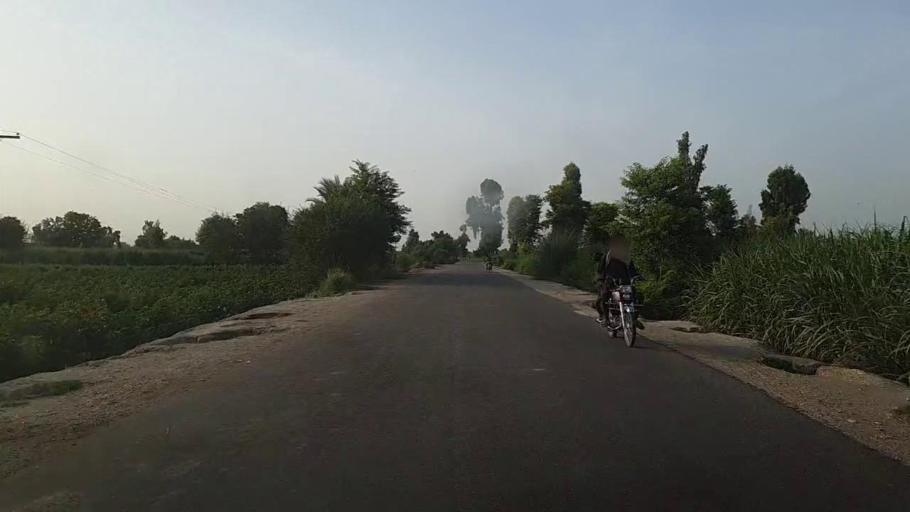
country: PK
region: Sindh
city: Ubauro
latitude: 28.1875
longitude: 69.8276
